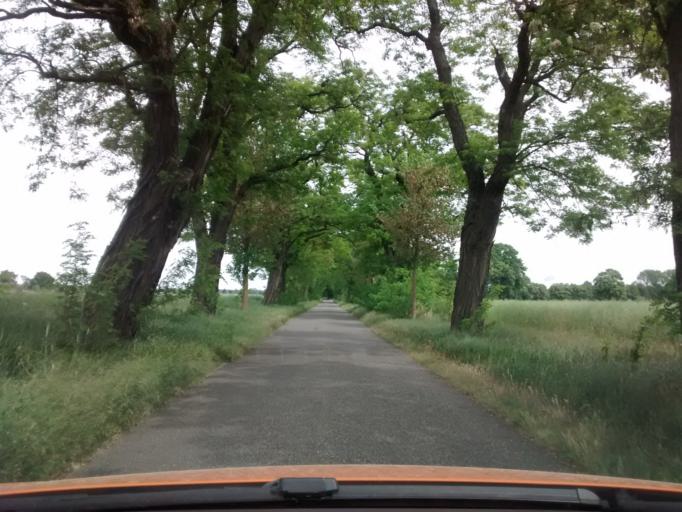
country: DE
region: Saxony-Anhalt
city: Holzdorf
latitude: 51.8365
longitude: 13.2050
